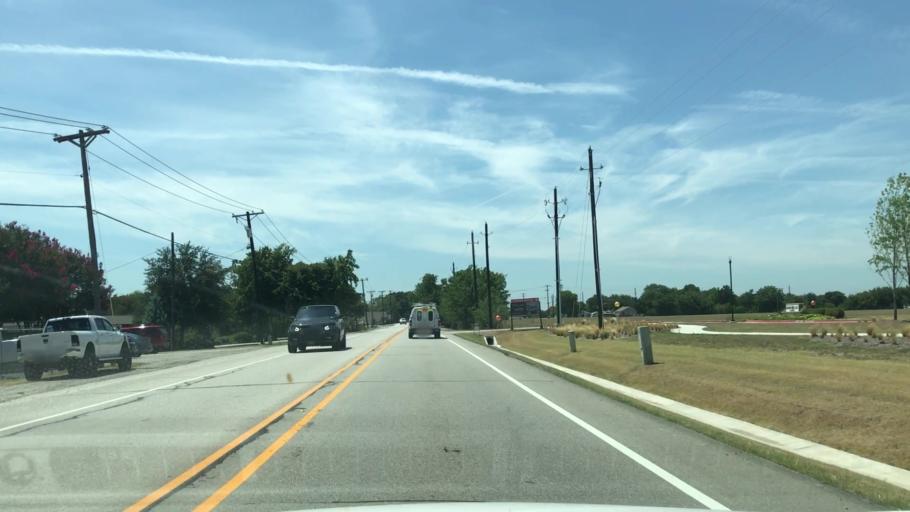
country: US
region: Texas
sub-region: Collin County
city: Fairview
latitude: 33.1609
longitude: -96.6309
